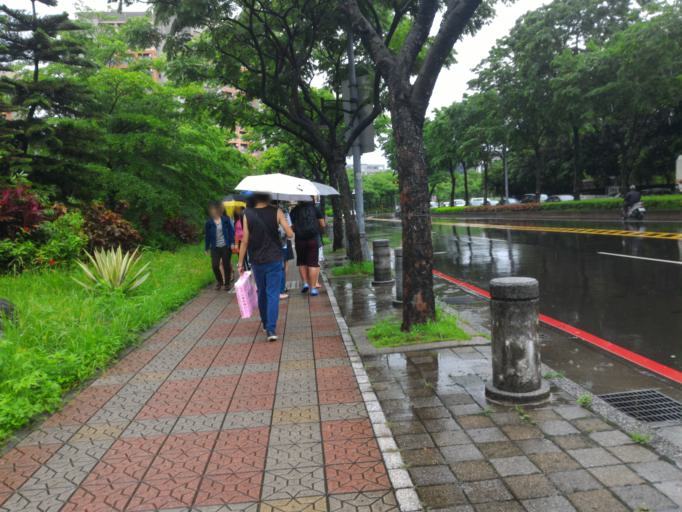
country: TW
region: Taiwan
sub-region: Taoyuan
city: Taoyuan
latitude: 24.9398
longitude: 121.3683
